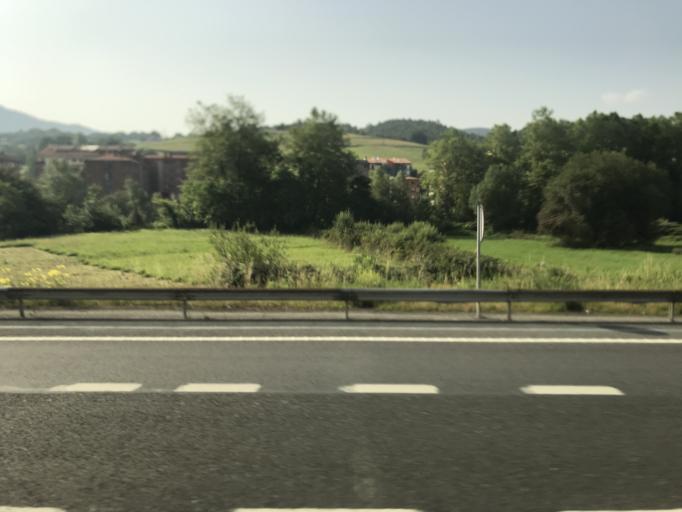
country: ES
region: Basque Country
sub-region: Provincia de Guipuzcoa
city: Andoain
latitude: 43.2118
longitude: -2.0320
